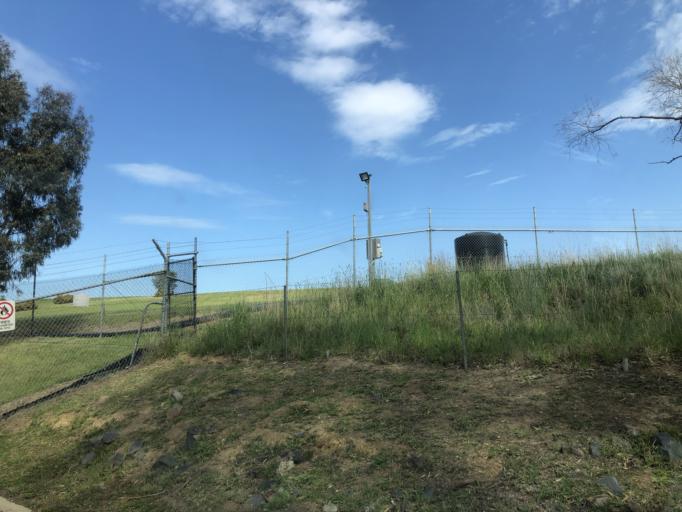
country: AU
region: Victoria
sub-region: Casey
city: Hampton Park
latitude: -38.0402
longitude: 145.2287
